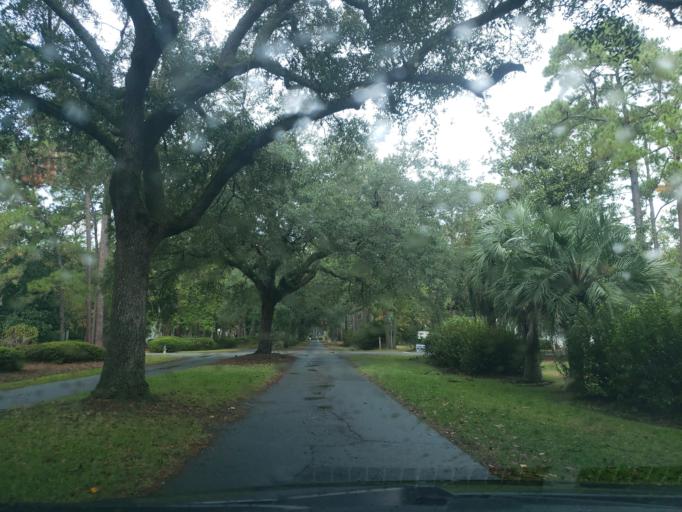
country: US
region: Georgia
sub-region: Chatham County
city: Isle of Hope
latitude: 31.9770
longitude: -81.0612
